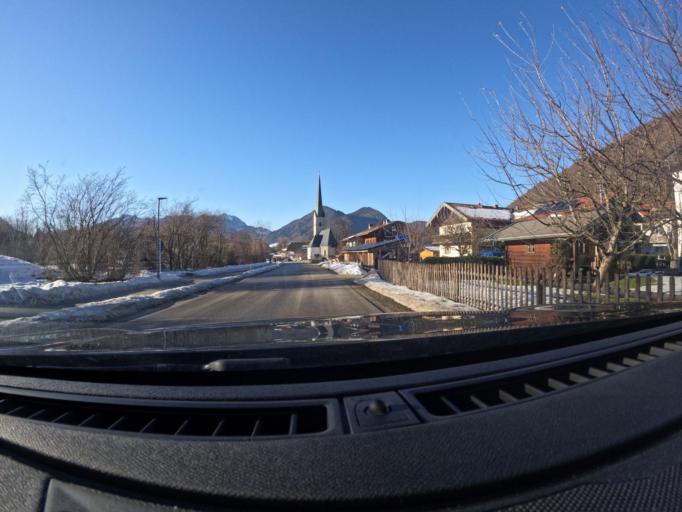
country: DE
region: Bavaria
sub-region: Upper Bavaria
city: Ruhpolding
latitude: 47.7561
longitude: 12.6646
